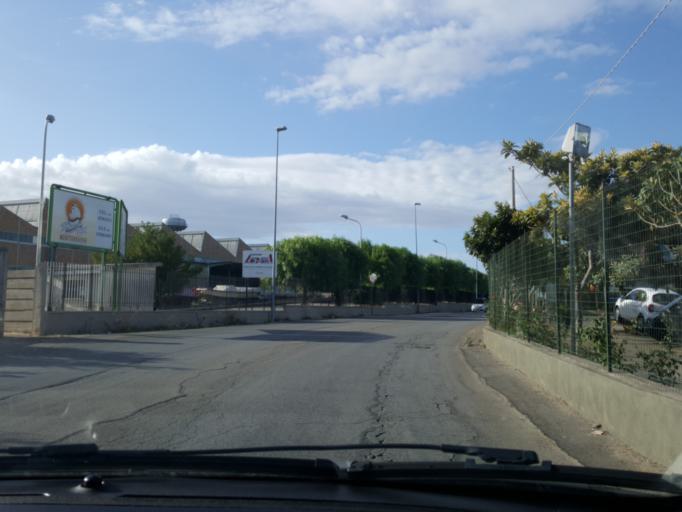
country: IT
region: Apulia
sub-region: Provincia di Bari
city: Triggiano
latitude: 41.0610
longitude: 16.9357
